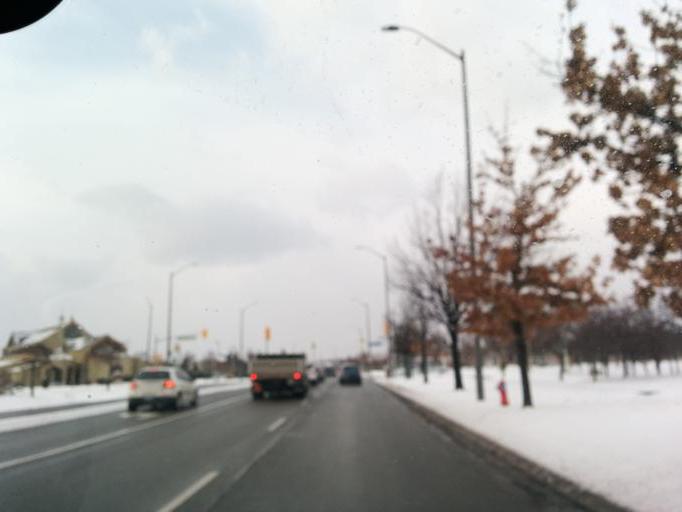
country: CA
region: Ontario
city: Mississauga
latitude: 43.5573
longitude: -79.7166
